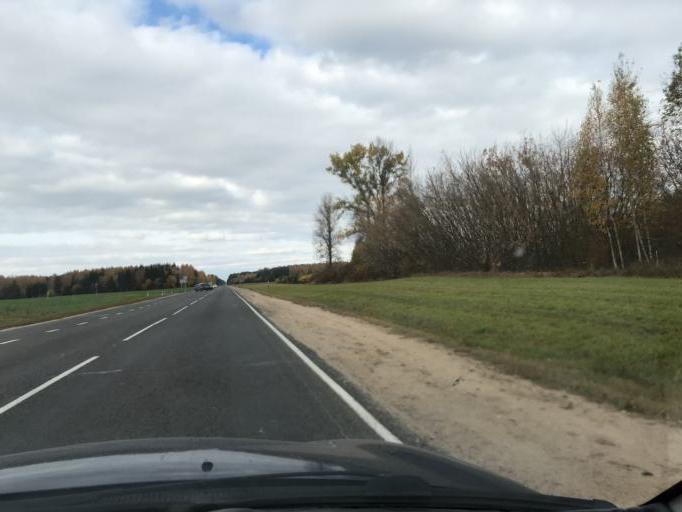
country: BY
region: Grodnenskaya
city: Lida
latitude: 53.9494
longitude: 25.2498
